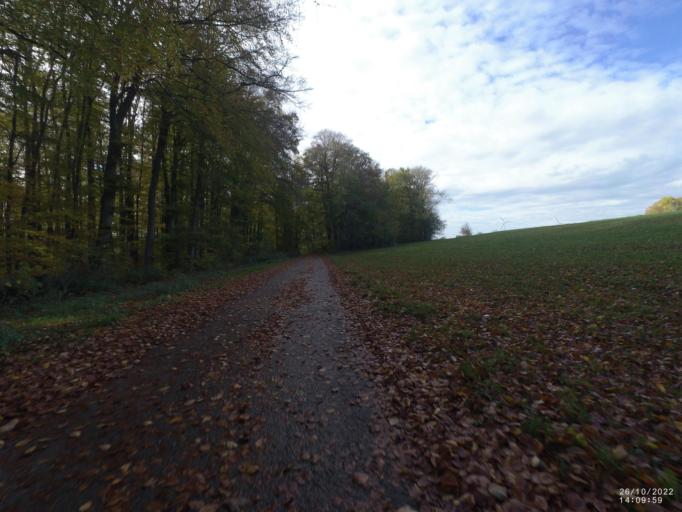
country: DE
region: Baden-Wuerttemberg
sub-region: Regierungsbezirk Stuttgart
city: Geislingen an der Steige
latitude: 48.6509
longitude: 9.8716
